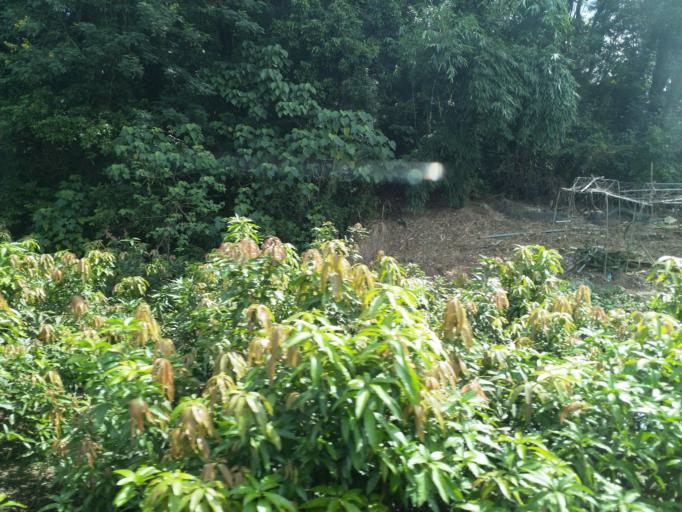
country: TW
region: Taiwan
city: Yujing
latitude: 22.9144
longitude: 120.5796
